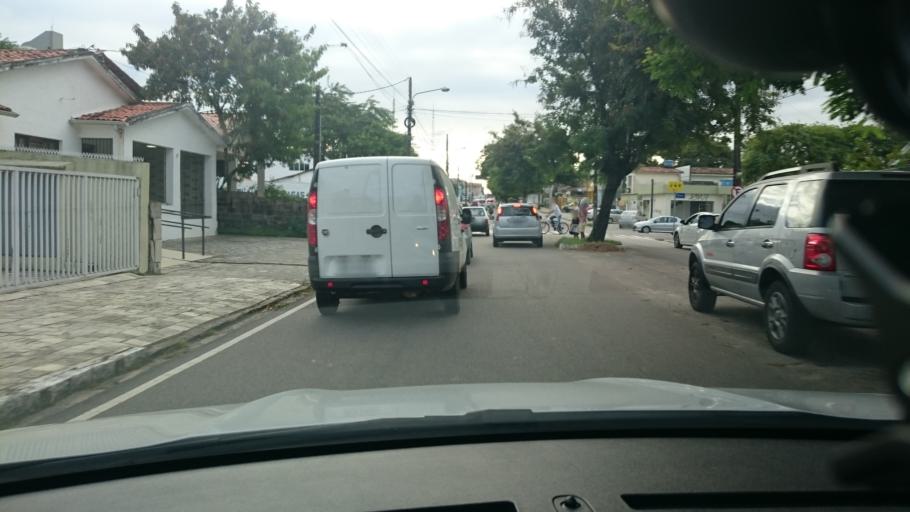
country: BR
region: Paraiba
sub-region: Joao Pessoa
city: Joao Pessoa
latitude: -7.1255
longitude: -34.8711
